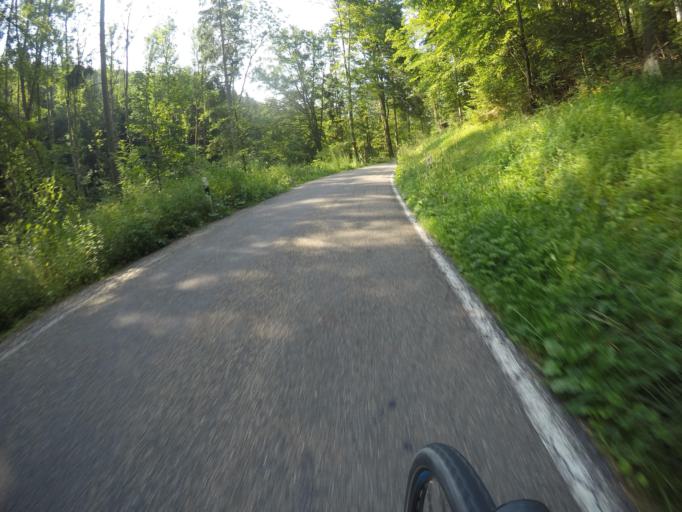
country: DE
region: Baden-Wuerttemberg
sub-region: Karlsruhe Region
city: Horb am Neckar
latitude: 48.4563
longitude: 8.7671
